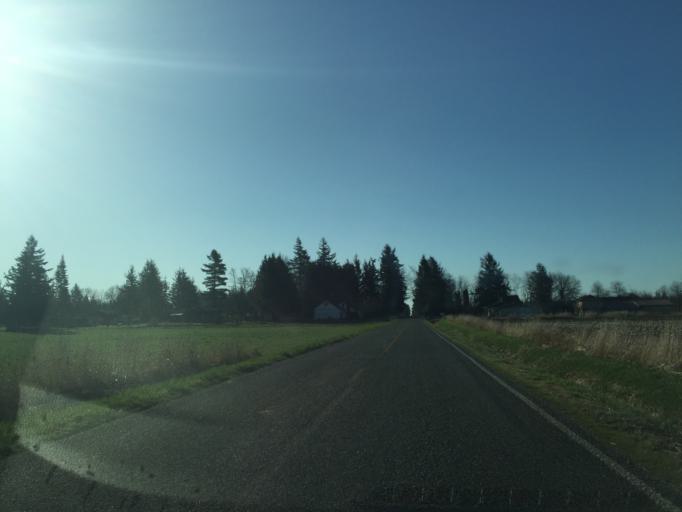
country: US
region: Washington
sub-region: Whatcom County
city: Lynden
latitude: 48.9008
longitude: -122.4967
